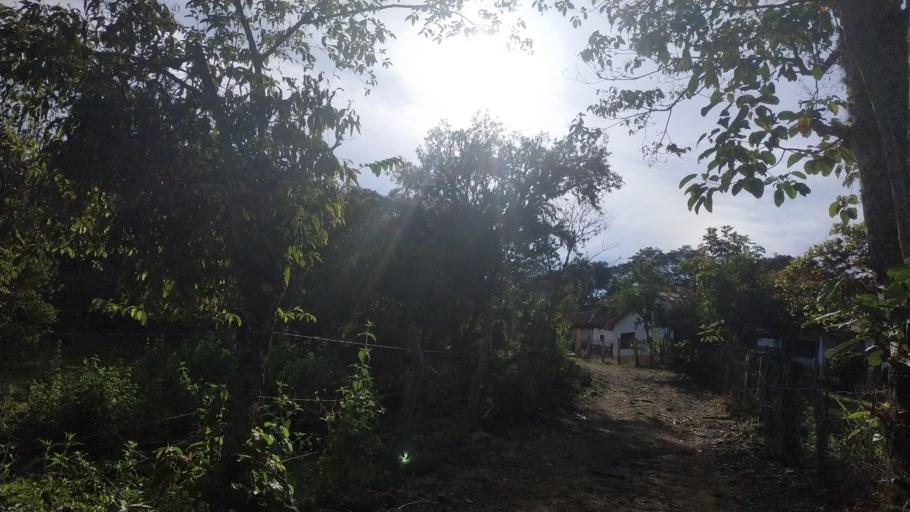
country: CO
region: Santander
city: Guepsa
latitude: 6.0239
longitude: -73.5285
